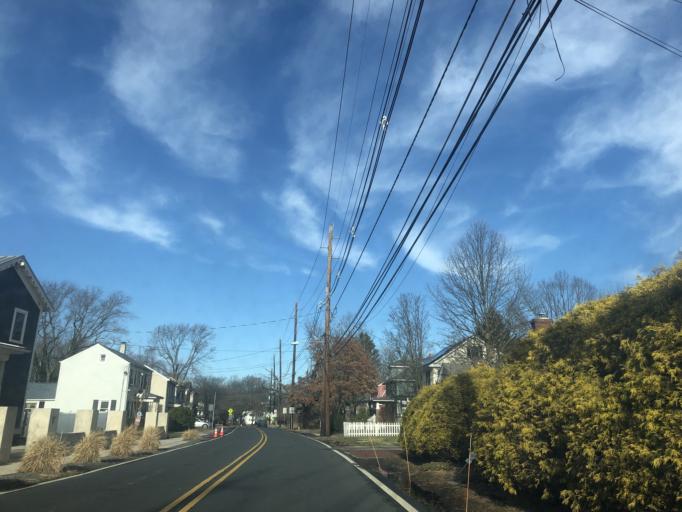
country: US
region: New Jersey
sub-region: Somerset County
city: Kingston
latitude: 40.3761
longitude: -74.6137
